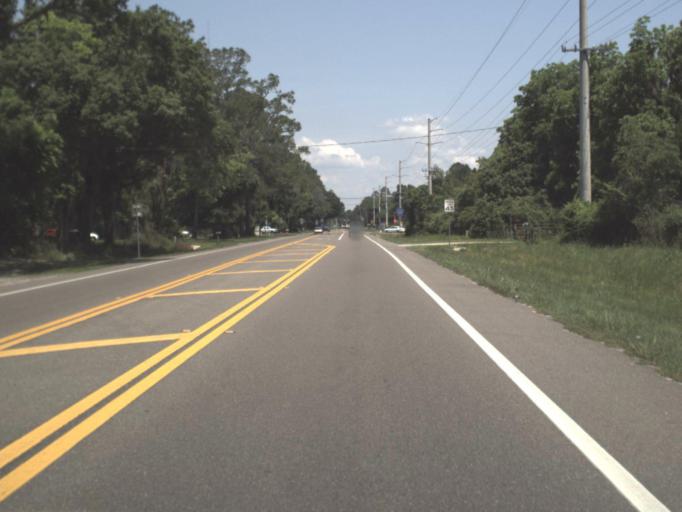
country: US
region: Florida
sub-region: Bradford County
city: Starke
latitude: 29.9256
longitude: -82.0998
